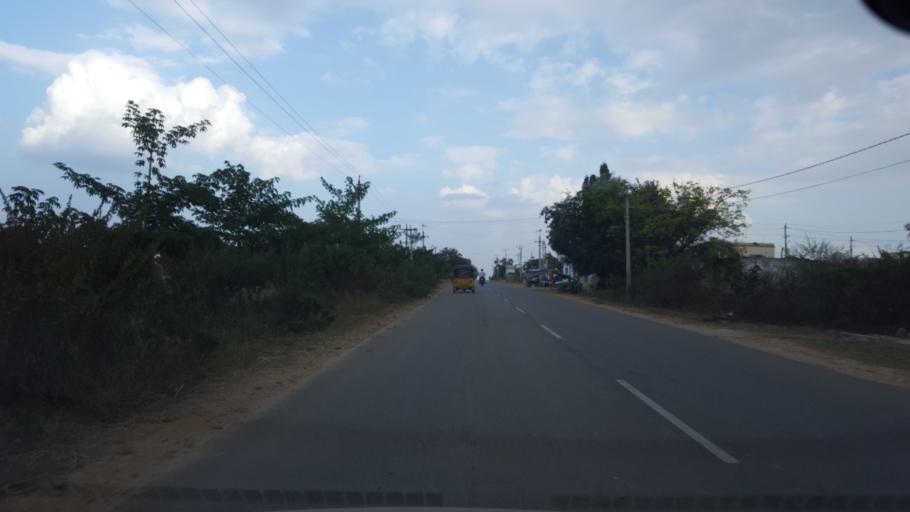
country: IN
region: Telangana
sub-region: Mahbubnagar
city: Mahbubnagar
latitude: 16.7602
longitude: 77.9566
